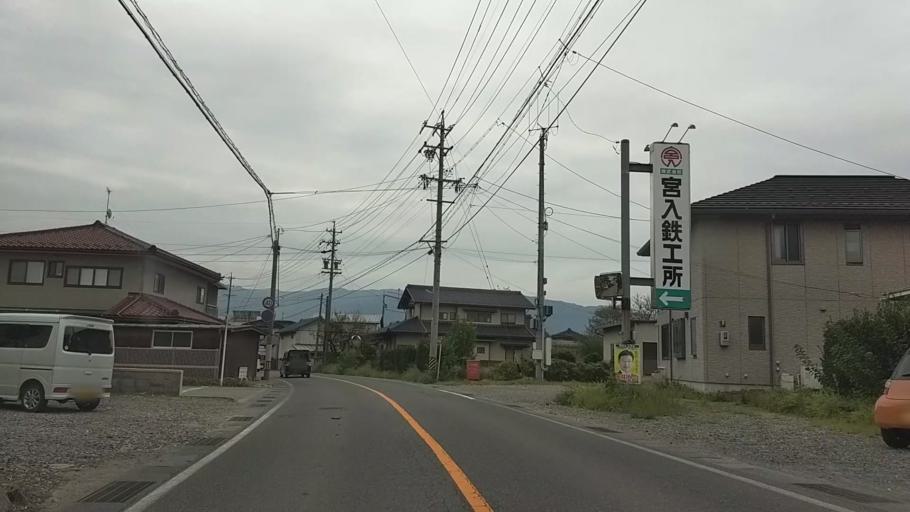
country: JP
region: Nagano
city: Nagano-shi
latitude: 36.5882
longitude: 138.1981
